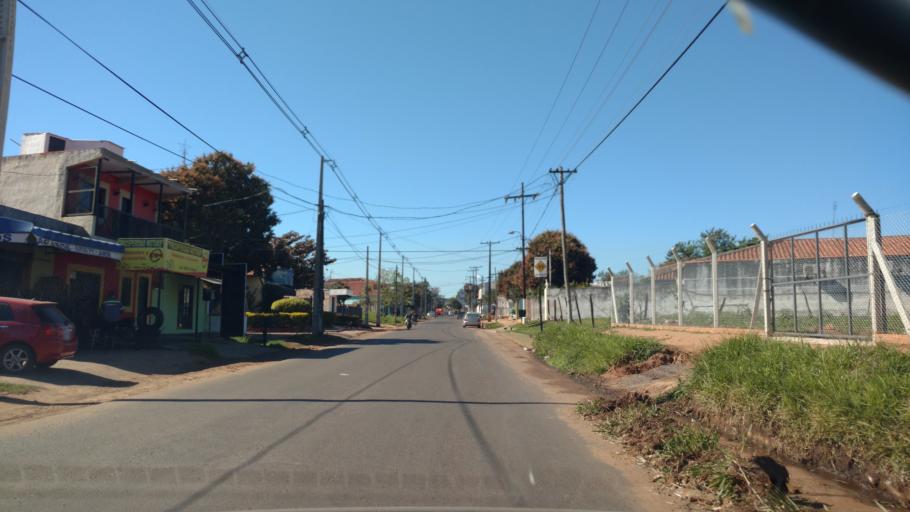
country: PY
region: Central
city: Itaugua
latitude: -25.3983
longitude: -57.3452
